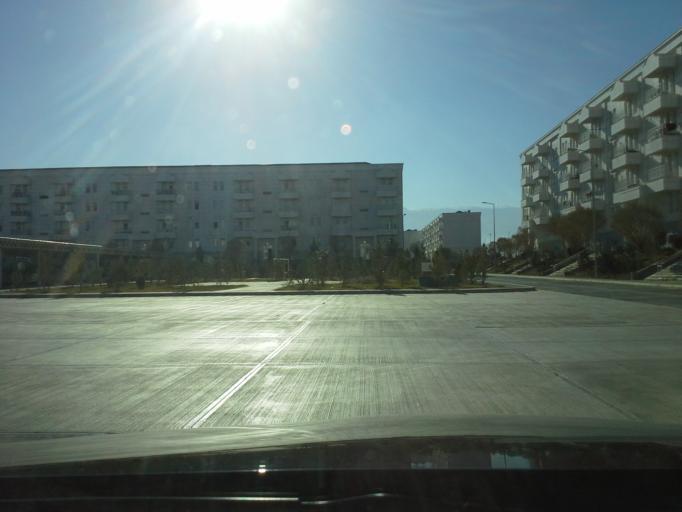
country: TM
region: Ahal
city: Ashgabat
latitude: 37.9756
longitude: 58.3412
